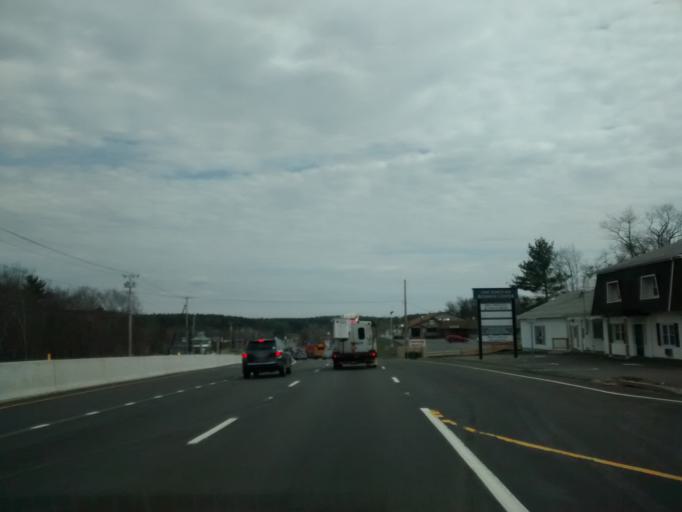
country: US
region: Massachusetts
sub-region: Worcester County
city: Sutton
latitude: 42.1627
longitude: -71.7411
